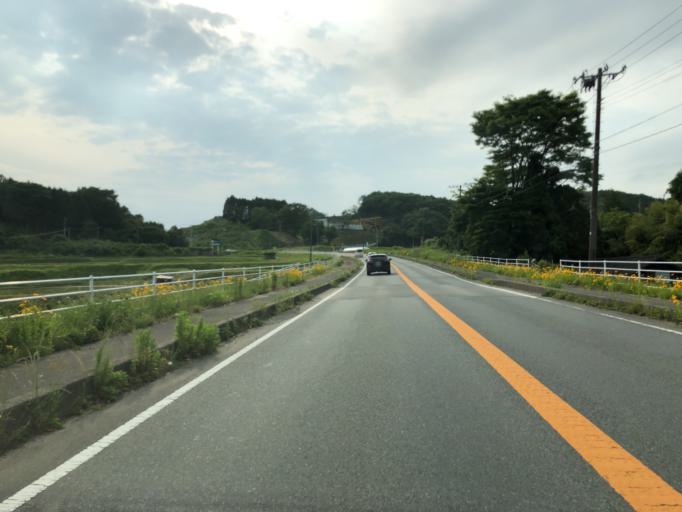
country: JP
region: Fukushima
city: Iwaki
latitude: 36.9999
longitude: 140.7975
